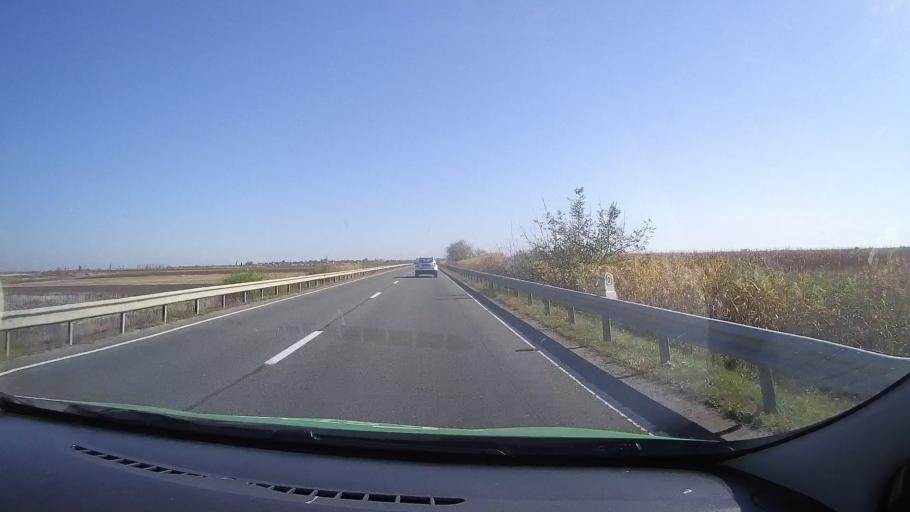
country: RO
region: Satu Mare
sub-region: Comuna Moftinu
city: Moftinu Mic
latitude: 47.6848
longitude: 22.5695
